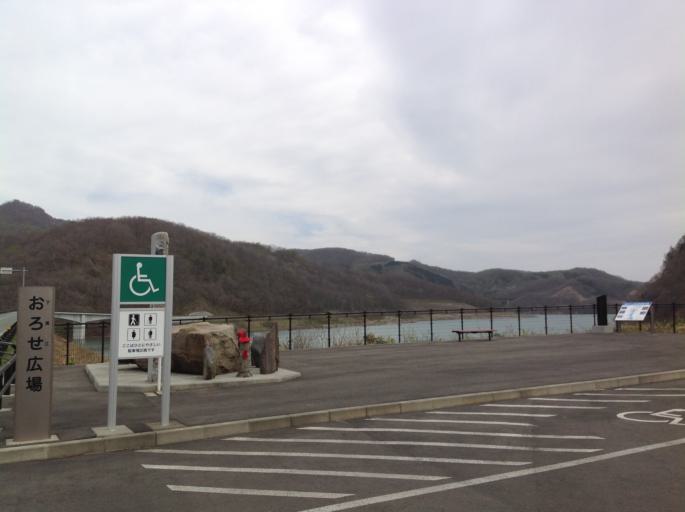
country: JP
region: Iwate
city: Mizusawa
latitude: 39.1023
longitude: 140.8821
